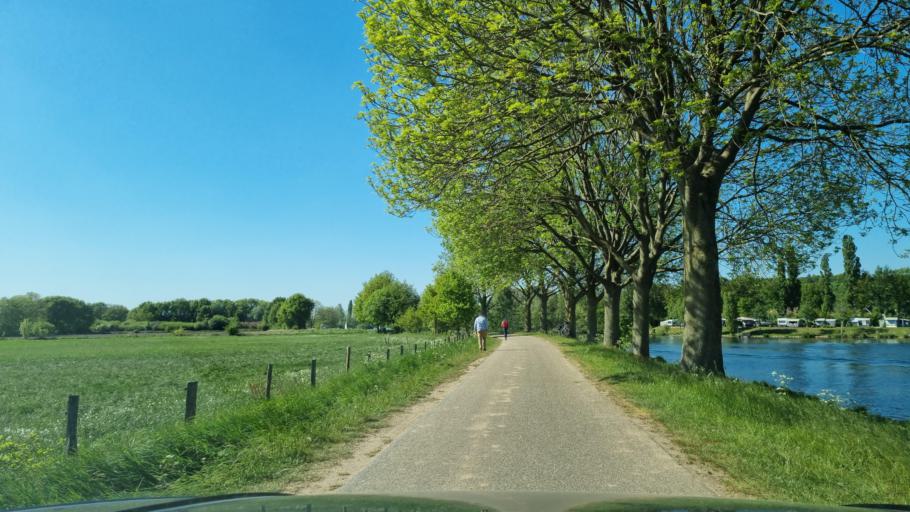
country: NL
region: North Brabant
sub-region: Gemeente Cuijk
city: Cuijk
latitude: 51.7338
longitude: 5.9102
